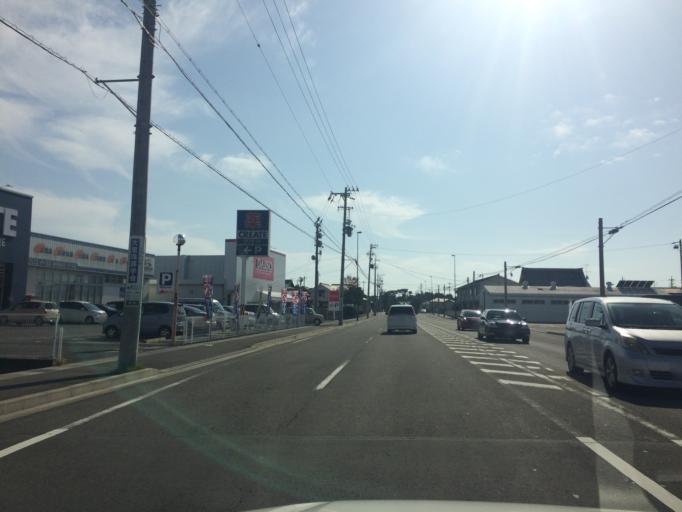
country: JP
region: Shizuoka
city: Shizuoka-shi
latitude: 34.9469
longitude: 138.4120
